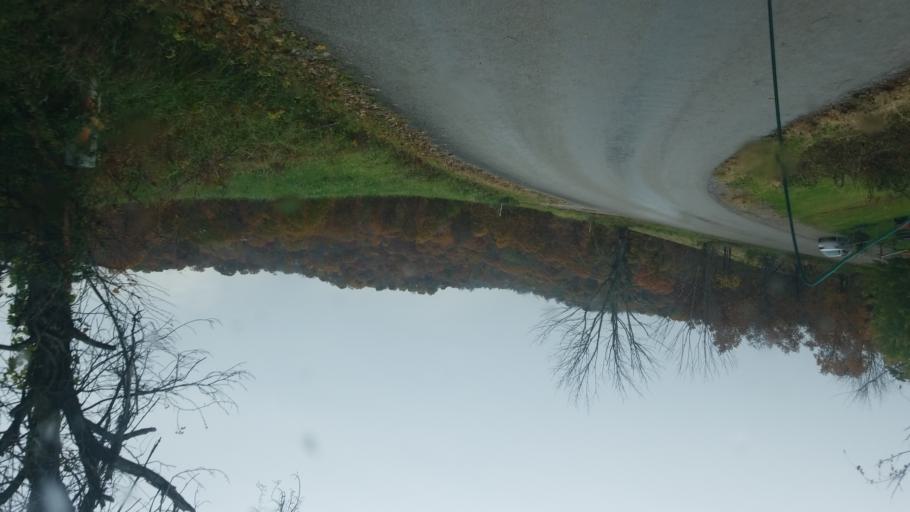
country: US
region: Ohio
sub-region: Washington County
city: Belpre
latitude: 39.3121
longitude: -81.5911
